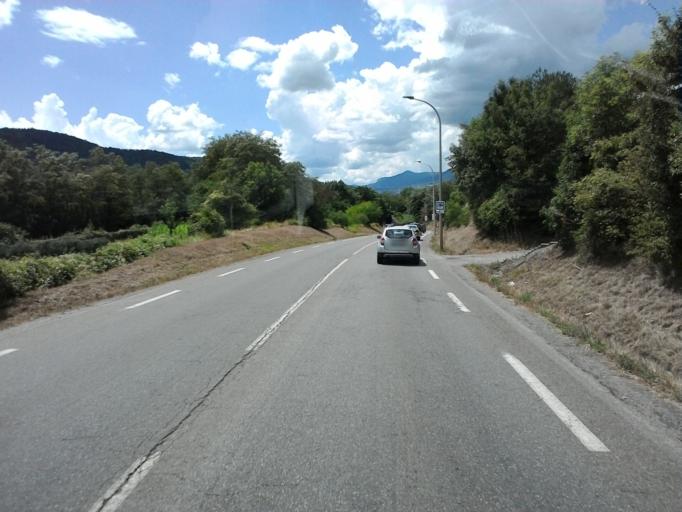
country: FR
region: Provence-Alpes-Cote d'Azur
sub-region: Departement des Hautes-Alpes
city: Gap
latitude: 44.5715
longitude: 6.1068
